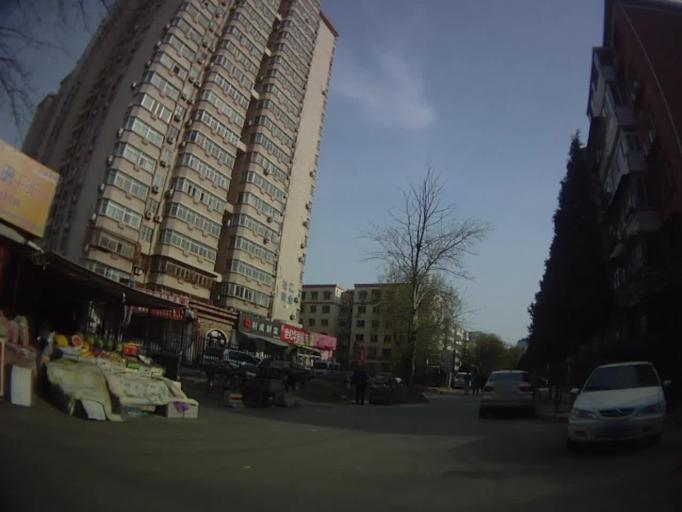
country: CN
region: Beijing
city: Chaowai
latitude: 39.8995
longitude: 116.4416
